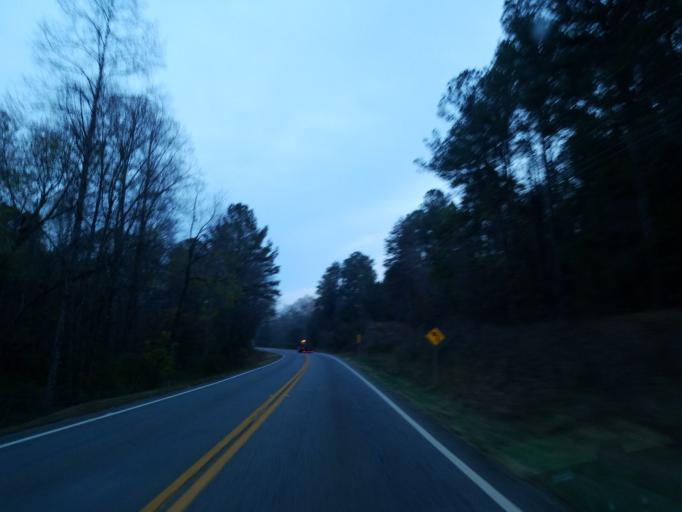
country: US
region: Georgia
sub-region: Pickens County
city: Jasper
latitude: 34.5151
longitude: -84.5667
